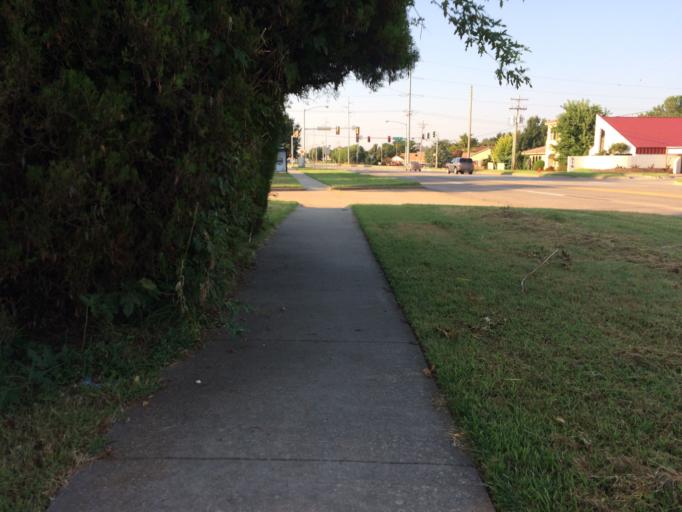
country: US
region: Oklahoma
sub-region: Cleveland County
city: Norman
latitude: 35.2124
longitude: -97.4765
